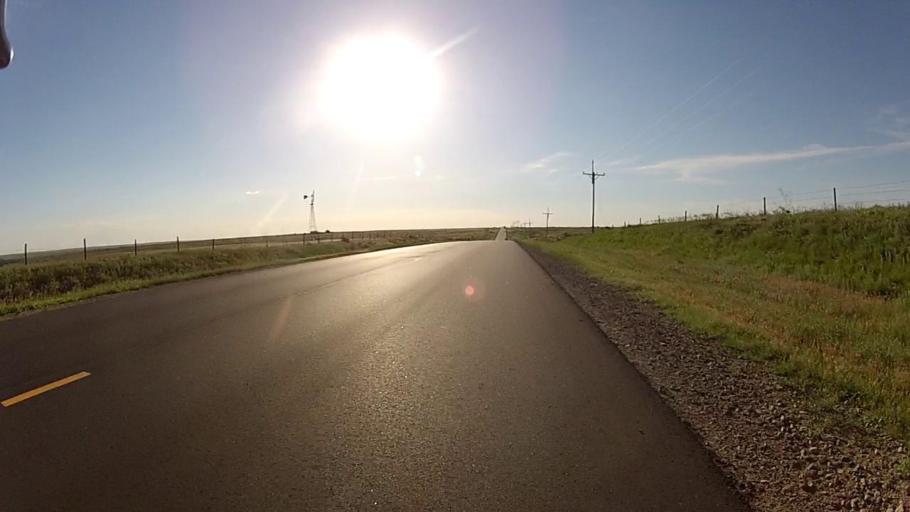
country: US
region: Kansas
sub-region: Comanche County
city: Coldwater
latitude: 37.2821
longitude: -99.1225
